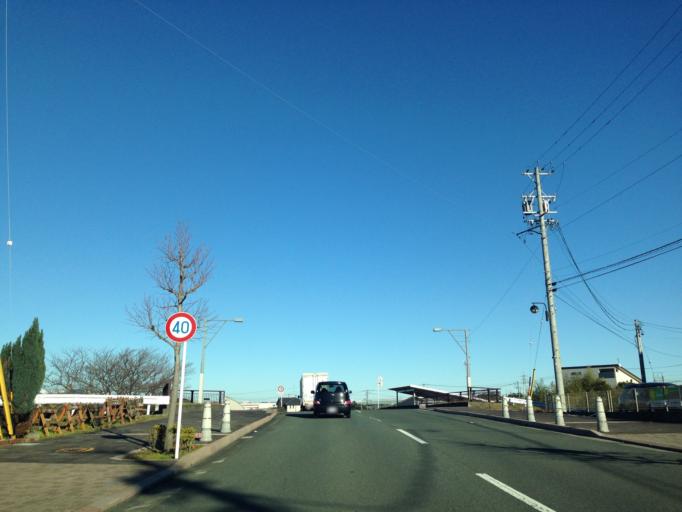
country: JP
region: Shizuoka
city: Fukuroi
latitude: 34.7540
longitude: 137.9638
